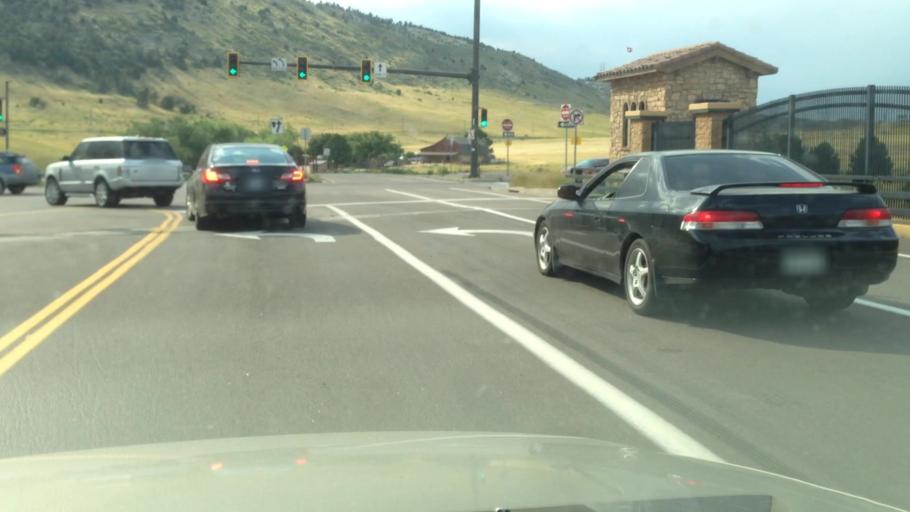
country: US
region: Colorado
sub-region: Jefferson County
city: West Pleasant View
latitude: 39.6872
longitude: -105.1880
